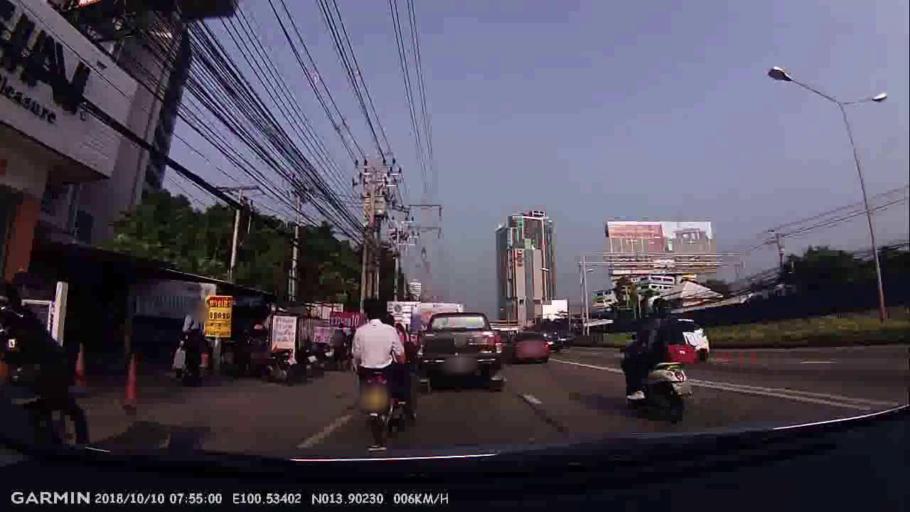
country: TH
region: Nonthaburi
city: Pak Kret
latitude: 13.9023
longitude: 100.5340
